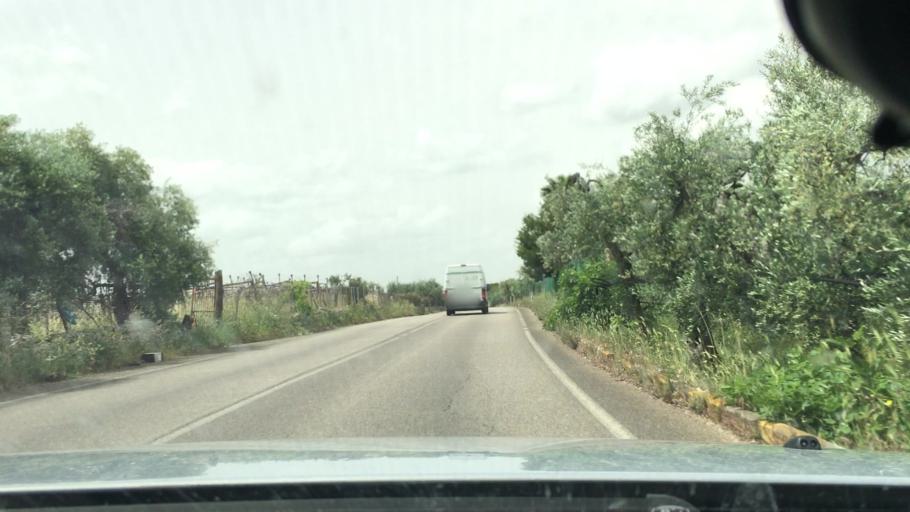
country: IT
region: Apulia
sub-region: Provincia di Bari
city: Capurso
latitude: 41.0425
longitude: 16.9402
